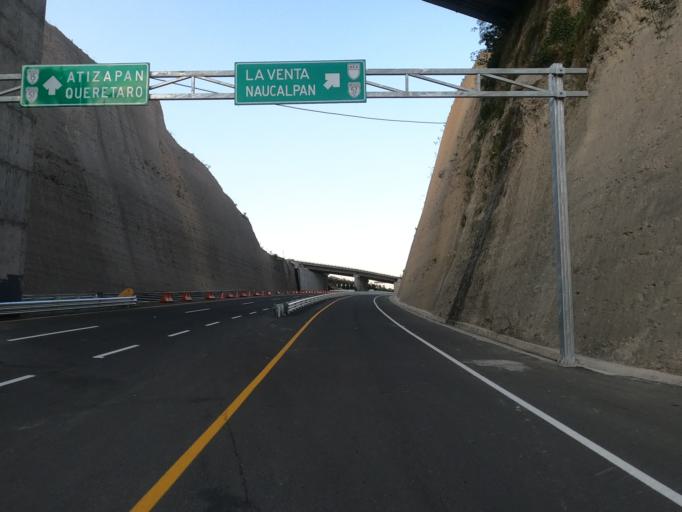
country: MX
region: Mexico
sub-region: Naucalpan de Juarez
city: Ejido el Castillo
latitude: 19.4361
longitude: -99.3034
